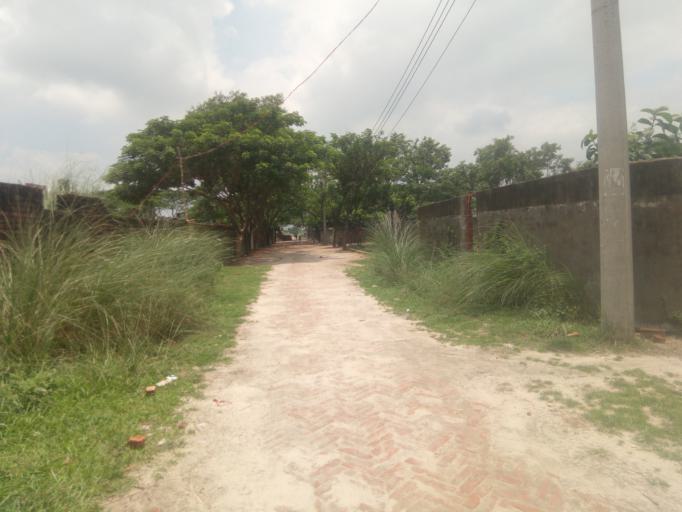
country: BD
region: Dhaka
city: Azimpur
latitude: 23.7551
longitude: 90.3503
